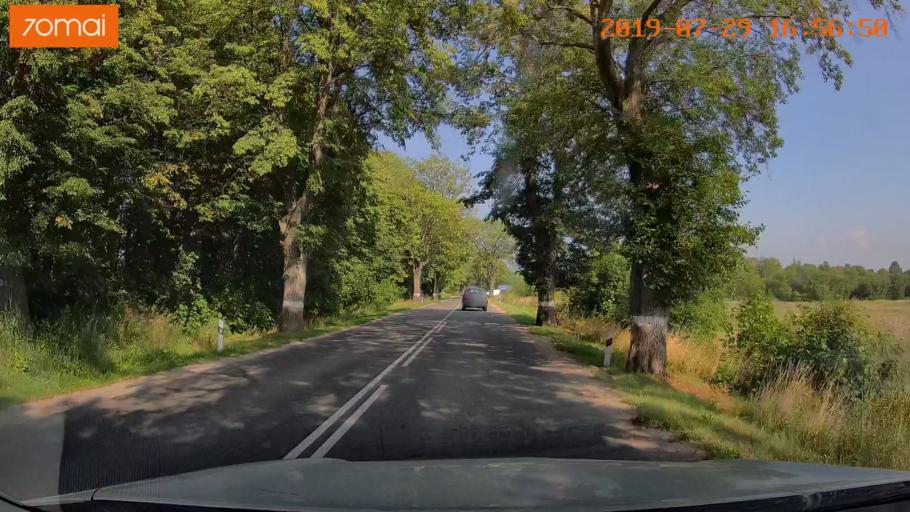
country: RU
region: Kaliningrad
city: Volochayevskoye
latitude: 54.8147
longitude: 20.1766
